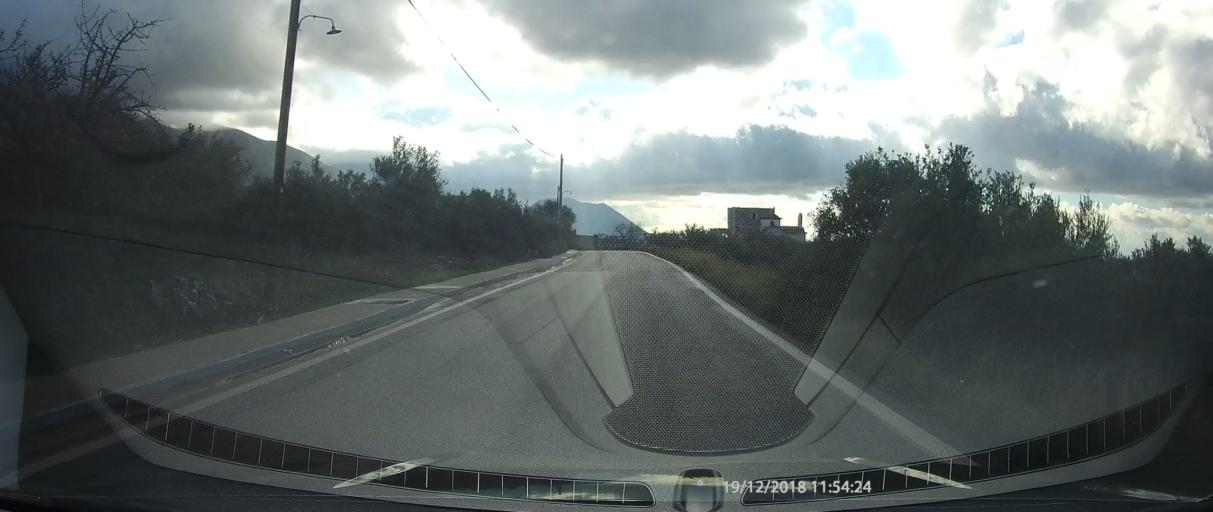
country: GR
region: Peloponnese
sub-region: Nomos Lakonias
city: Gytheio
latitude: 36.6189
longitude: 22.3905
